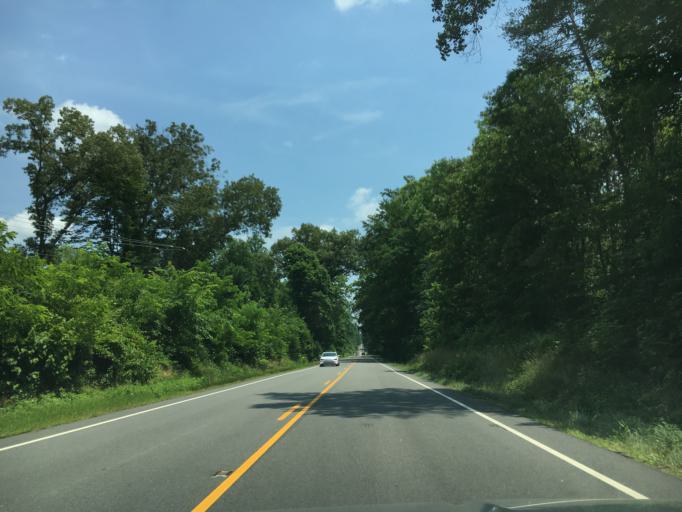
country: US
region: Virginia
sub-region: Cumberland County
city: Cumberland
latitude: 37.4860
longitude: -78.3274
